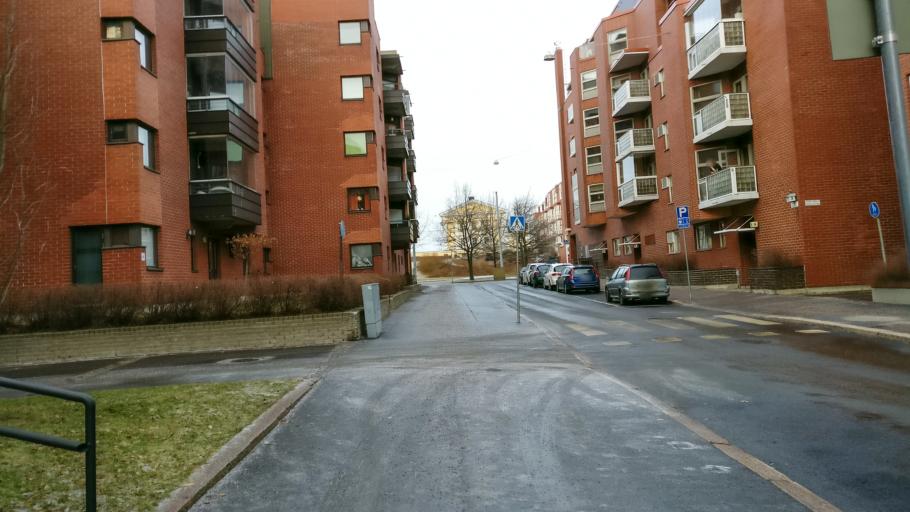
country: FI
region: Uusimaa
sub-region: Helsinki
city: Helsinki
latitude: 60.1668
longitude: 24.9753
